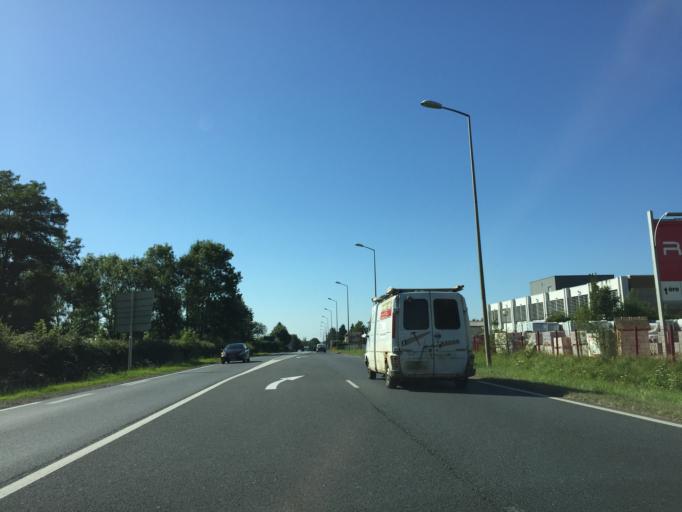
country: FR
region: Lower Normandy
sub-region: Departement du Calvados
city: Beuvillers
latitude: 49.1464
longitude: 0.2597
